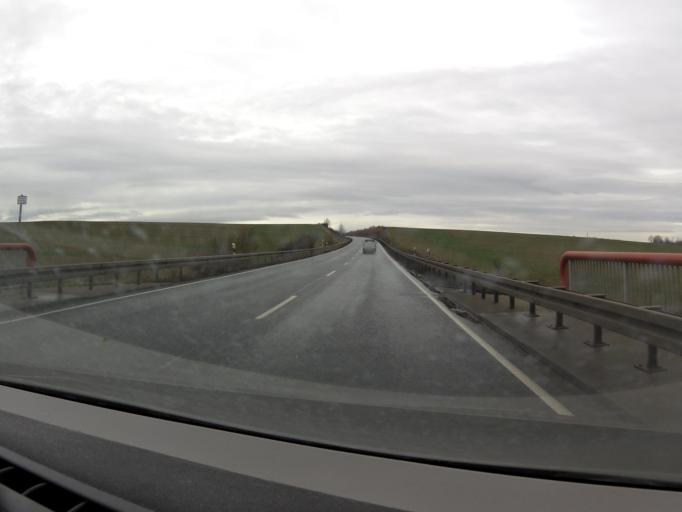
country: DE
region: Saxony-Anhalt
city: Grossorner
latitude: 51.6432
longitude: 11.4752
